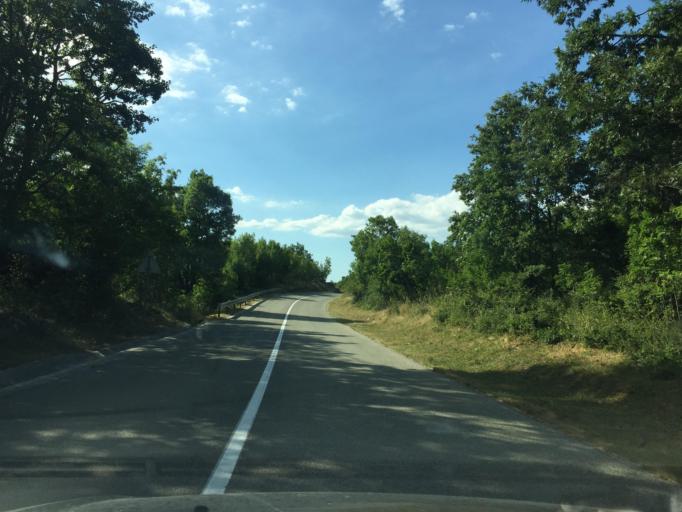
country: HR
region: Primorsko-Goranska
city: Klana
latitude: 45.4562
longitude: 14.3140
